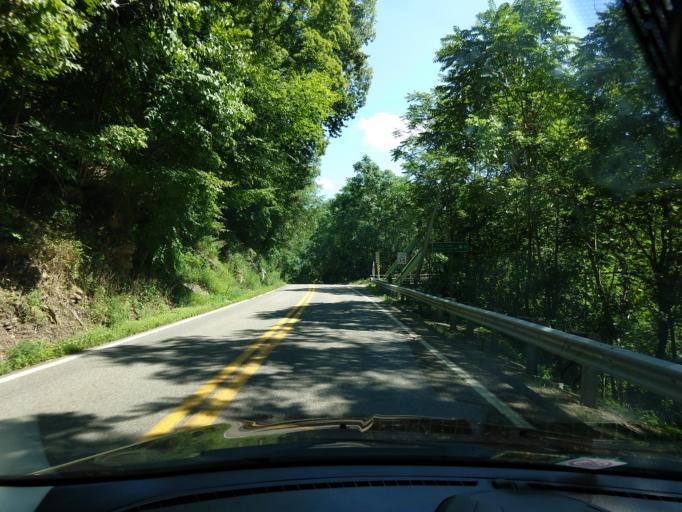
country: US
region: West Virginia
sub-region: Fayette County
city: Ansted
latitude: 38.1385
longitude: -81.2148
